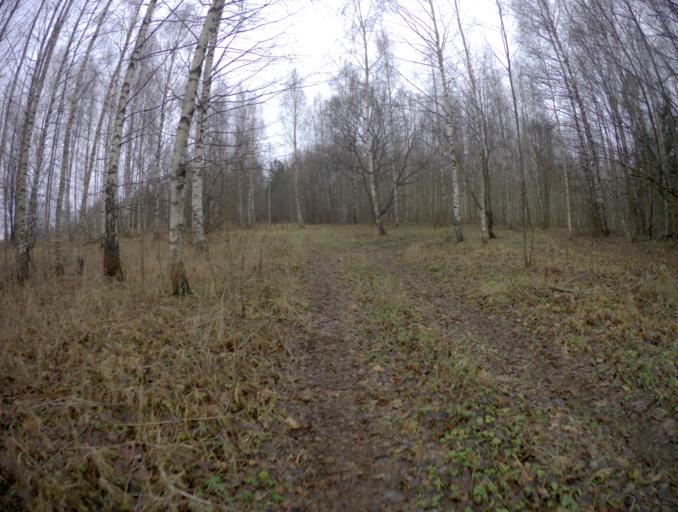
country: RU
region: Vladimir
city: Golovino
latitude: 56.0083
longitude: 40.5409
